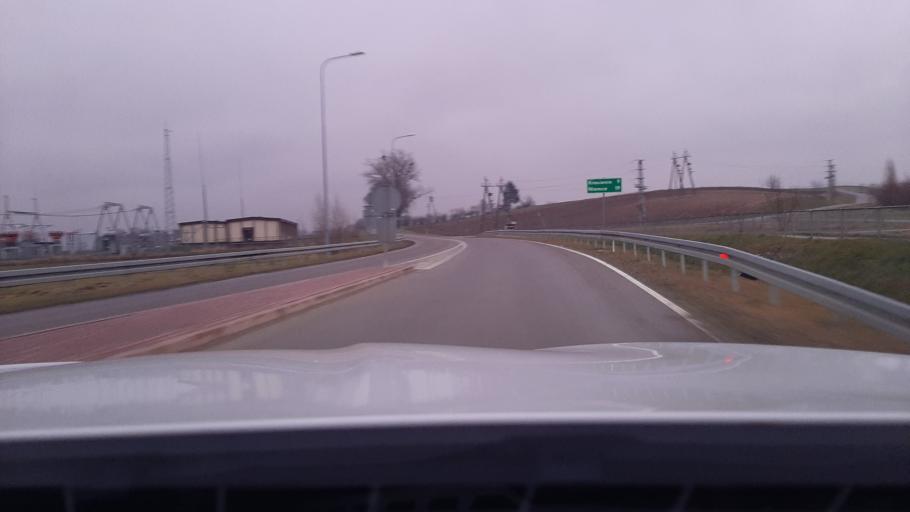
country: PL
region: Lublin Voivodeship
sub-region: Powiat lubelski
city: Garbow
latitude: 51.3480
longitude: 22.3710
